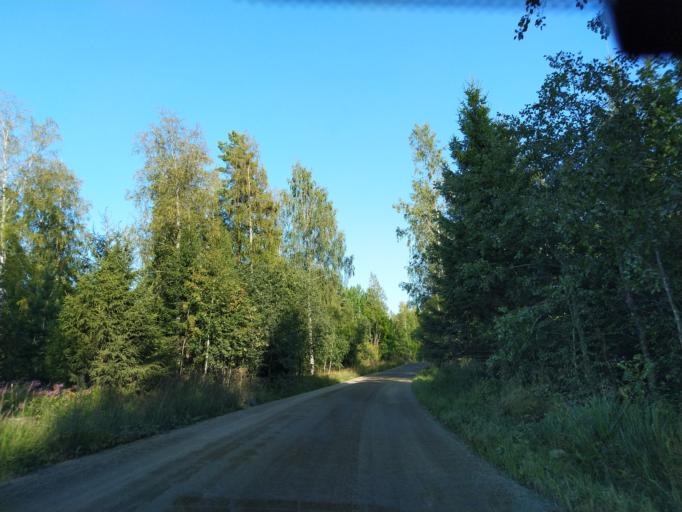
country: FI
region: Central Finland
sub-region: Jaemsae
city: Kuhmoinen
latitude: 61.6037
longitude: 25.1439
